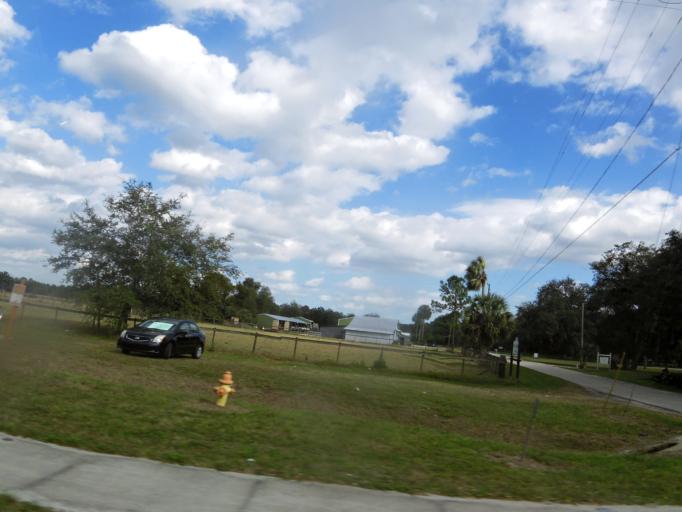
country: US
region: Florida
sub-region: Volusia County
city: Pierson
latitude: 29.2239
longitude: -81.4606
